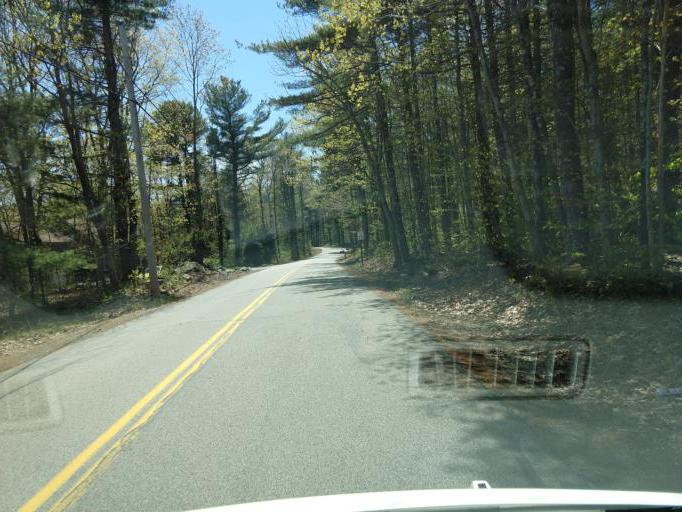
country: US
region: Maine
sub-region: York County
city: Cape Neddick
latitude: 43.2222
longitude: -70.6393
